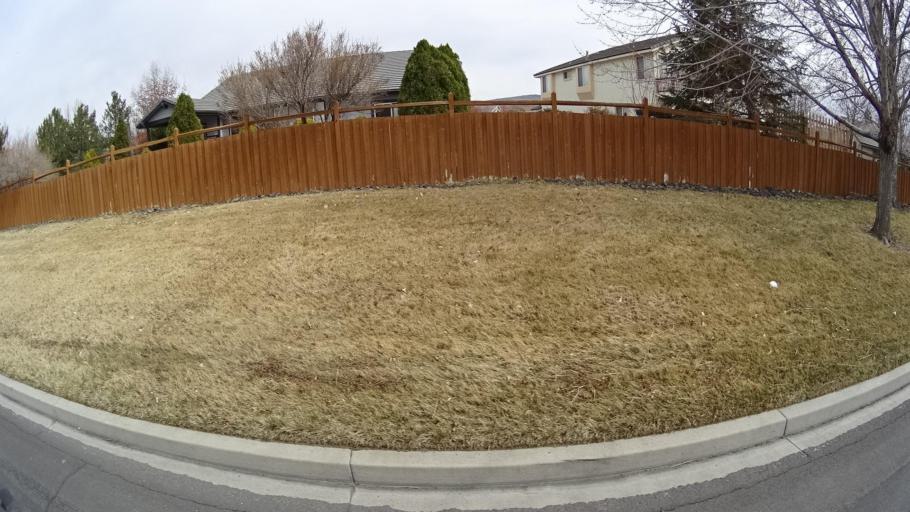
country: US
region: Nevada
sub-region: Washoe County
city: Spanish Springs
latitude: 39.6200
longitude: -119.6794
